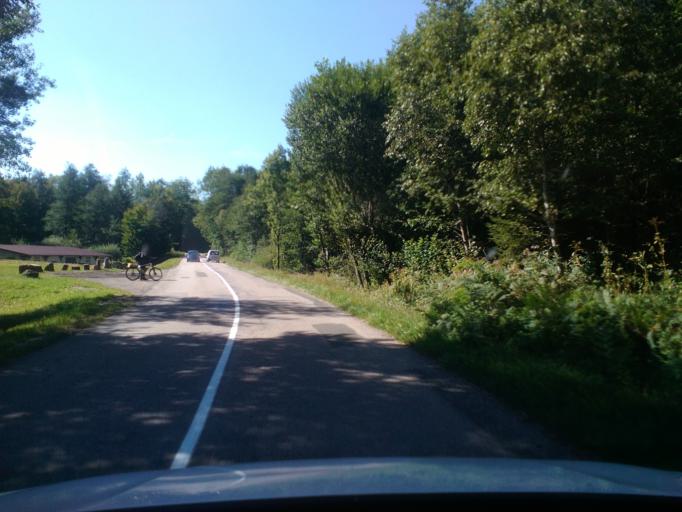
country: FR
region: Lorraine
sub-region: Departement des Vosges
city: Senones
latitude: 48.4190
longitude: 7.0042
